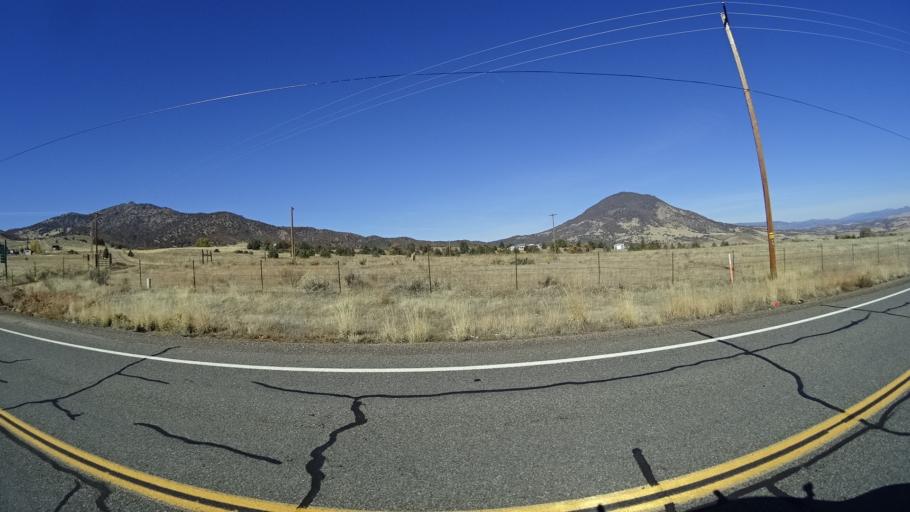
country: US
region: California
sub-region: Siskiyou County
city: Montague
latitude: 41.8044
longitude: -122.5043
